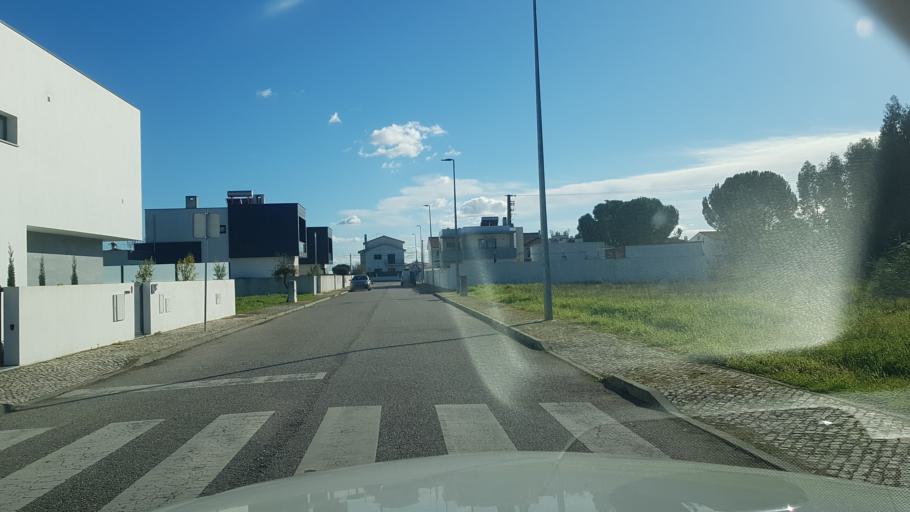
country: PT
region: Santarem
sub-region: Entroncamento
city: Entroncamento
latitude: 39.4788
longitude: -8.4781
